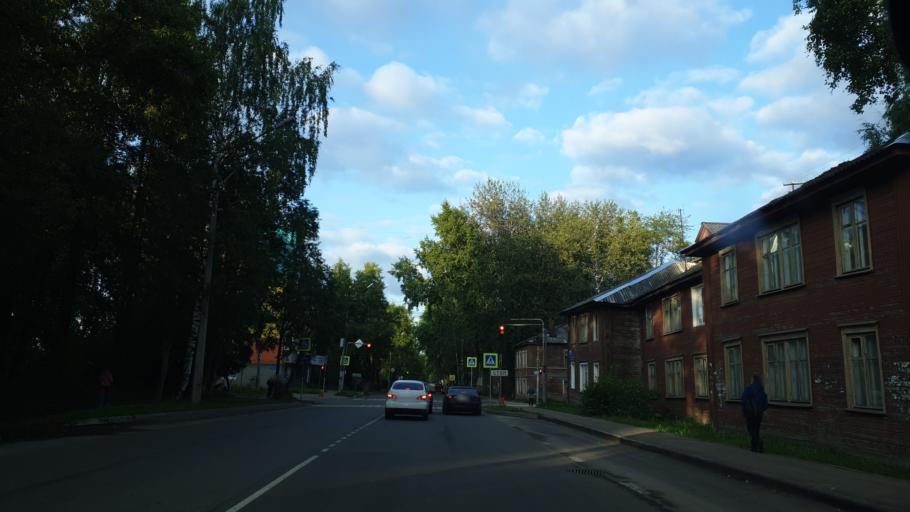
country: RU
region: Komi Republic
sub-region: Syktyvdinskiy Rayon
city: Syktyvkar
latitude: 61.6655
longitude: 50.8018
